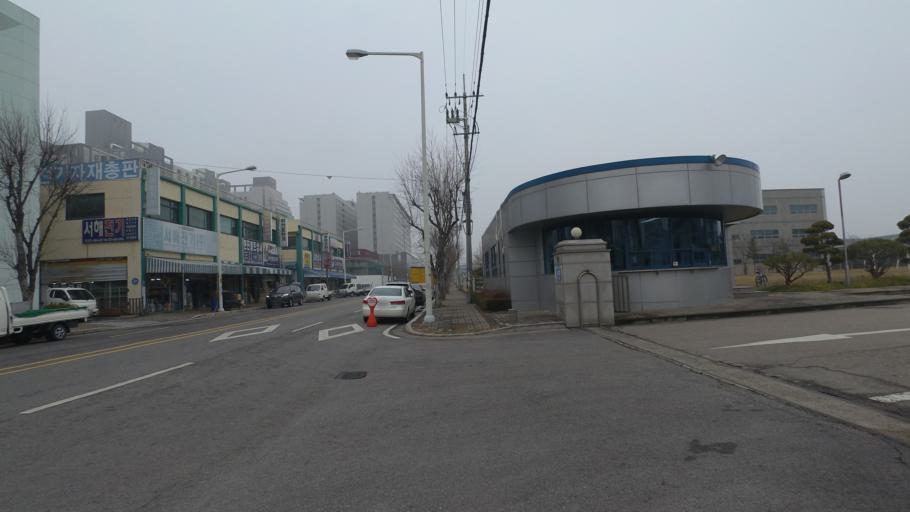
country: KR
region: Chungcheongnam-do
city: Tangjin
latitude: 36.9752
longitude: 126.8455
